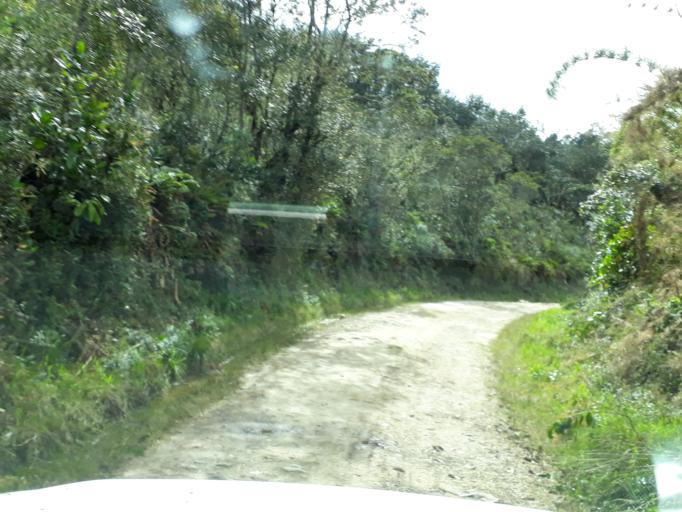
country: CO
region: Cundinamarca
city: Junin
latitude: 4.7868
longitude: -73.7743
